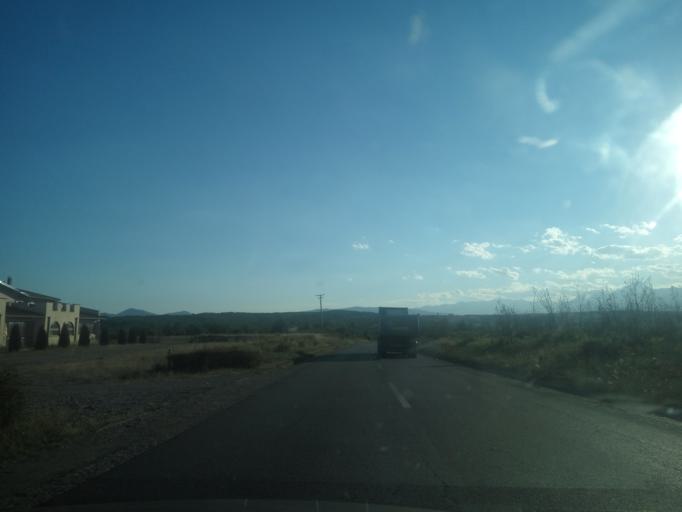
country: XK
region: Gjakova
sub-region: Komuna e Gjakoves
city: Gjakove
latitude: 42.4363
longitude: 20.4753
